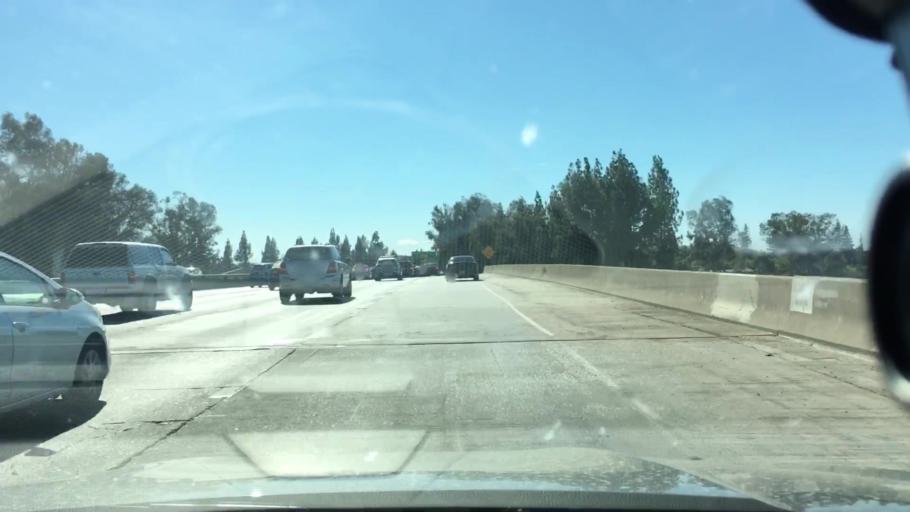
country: US
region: California
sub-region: Sacramento County
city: Sacramento
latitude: 38.6005
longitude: -121.4397
